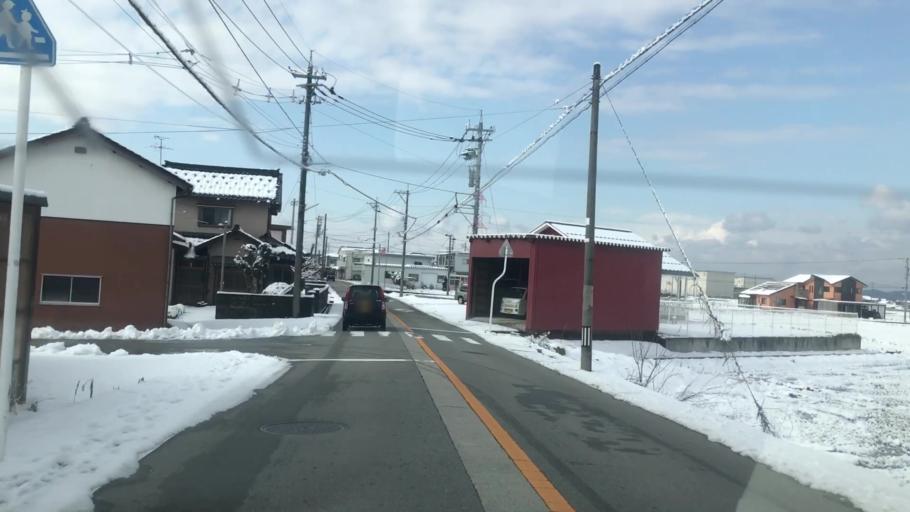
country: JP
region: Toyama
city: Toyama-shi
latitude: 36.6324
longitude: 137.2170
